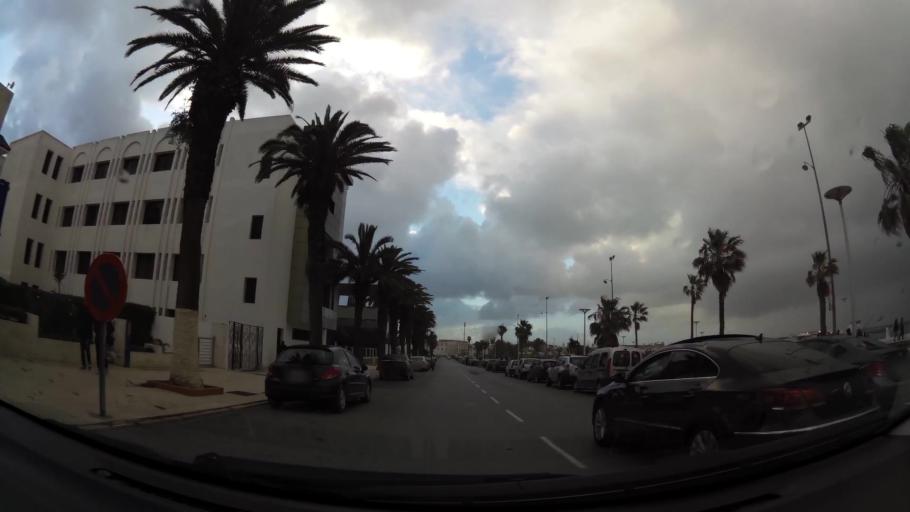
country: MA
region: Doukkala-Abda
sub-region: El-Jadida
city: El Jadida
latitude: 33.2504
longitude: -8.4994
